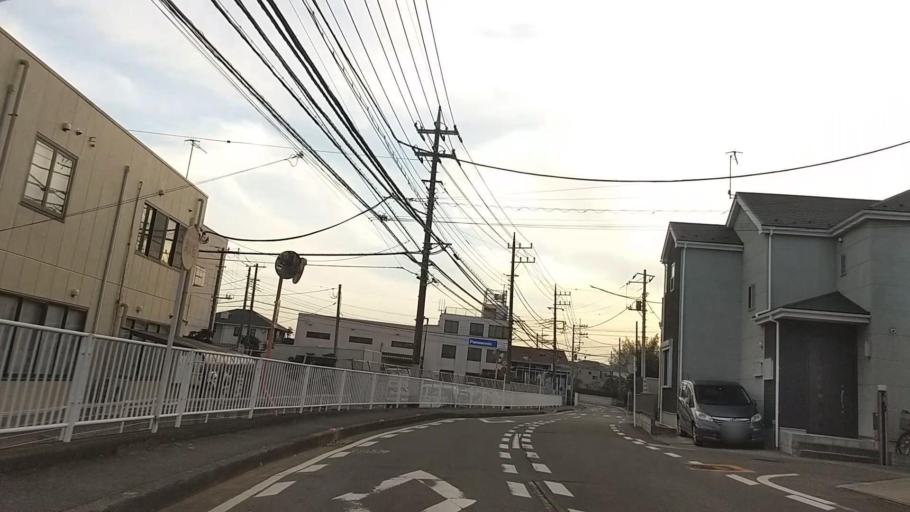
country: JP
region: Kanagawa
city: Atsugi
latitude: 35.4426
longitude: 139.3541
